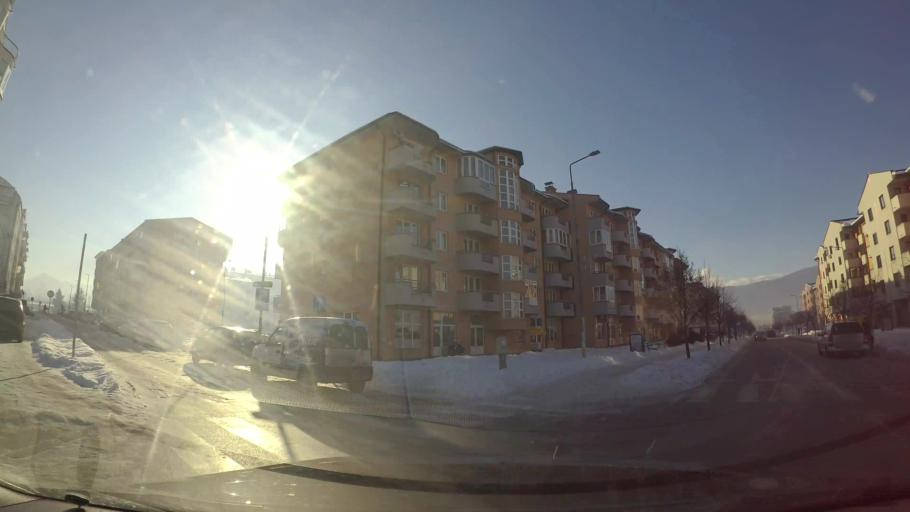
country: BA
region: Federation of Bosnia and Herzegovina
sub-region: Kanton Sarajevo
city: Sarajevo
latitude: 43.8217
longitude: 18.3634
